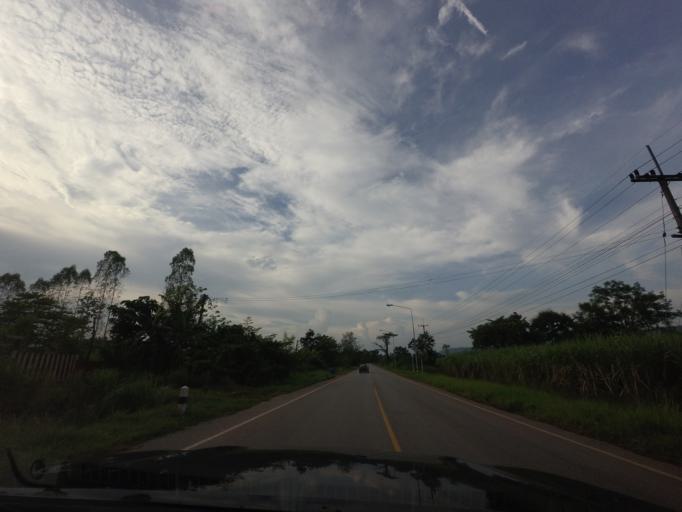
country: TH
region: Changwat Udon Thani
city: Nam Som
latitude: 17.8318
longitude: 102.2619
